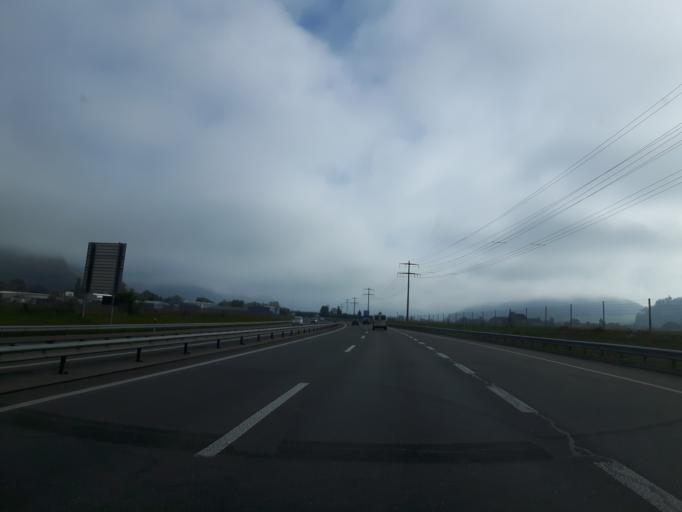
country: CH
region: Lucerne
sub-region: Willisau District
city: Reiden
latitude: 47.2410
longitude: 7.9580
